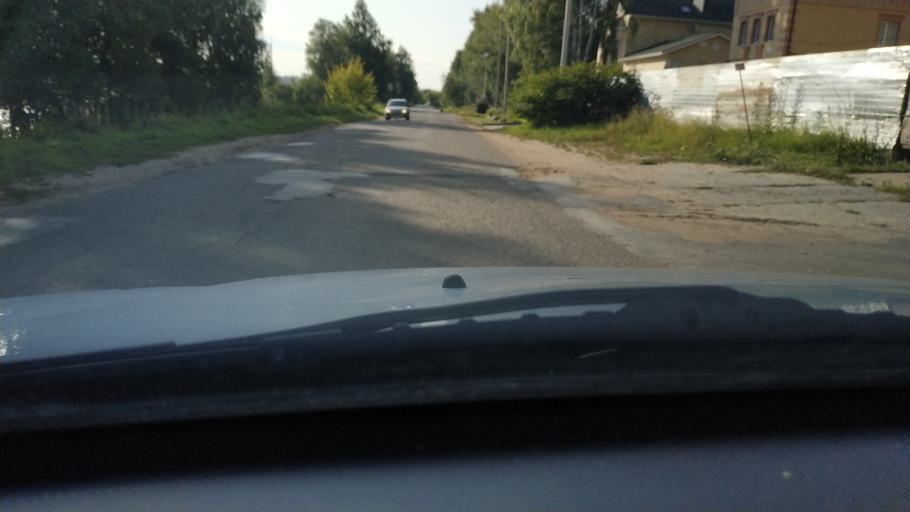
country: RU
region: Kostroma
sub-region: Kostromskoy Rayon
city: Kostroma
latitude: 57.7544
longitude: 40.9202
